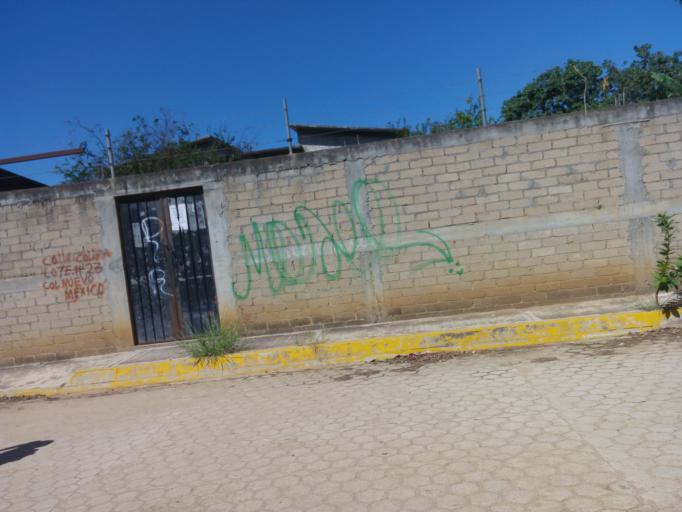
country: MX
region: Oaxaca
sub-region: Santa Maria Atzompa
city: La Canada
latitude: 17.0833
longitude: -96.7530
